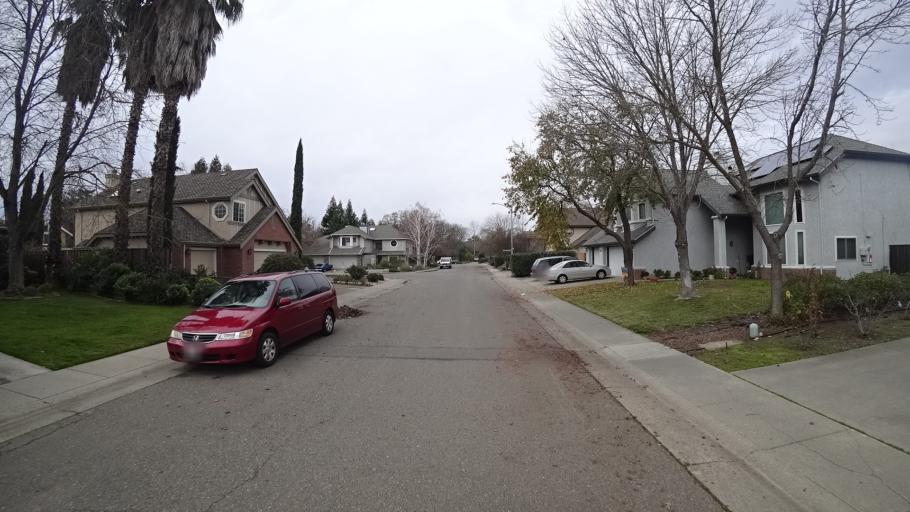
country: US
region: California
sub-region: Yolo County
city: Davis
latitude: 38.5643
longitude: -121.7239
